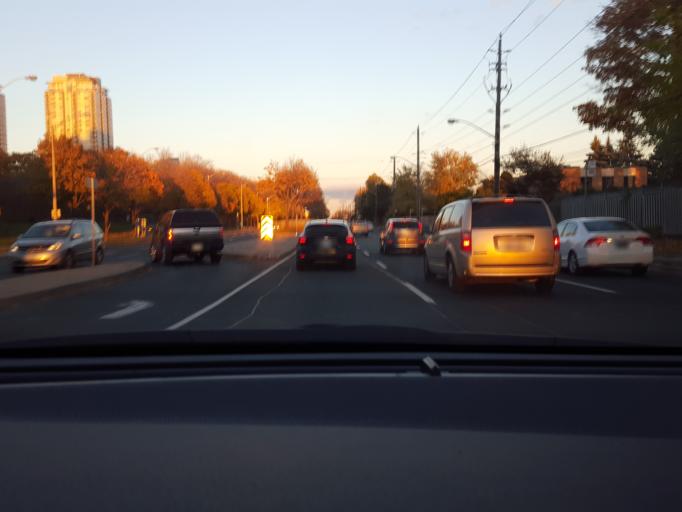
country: CA
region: Ontario
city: Scarborough
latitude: 43.7706
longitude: -79.2586
